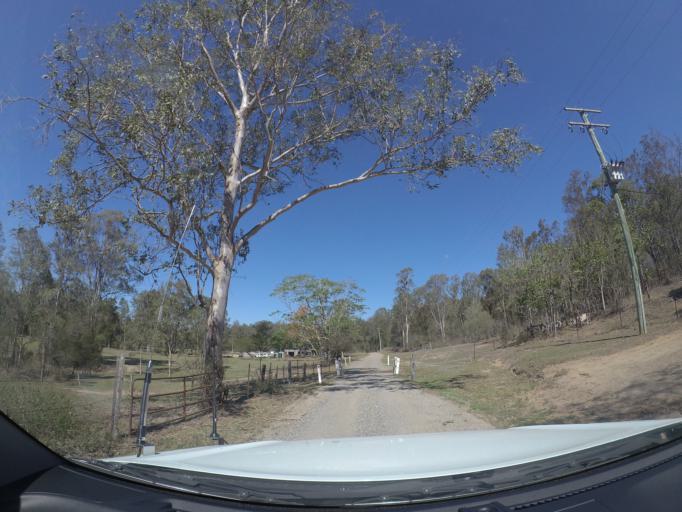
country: AU
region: Queensland
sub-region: Ipswich
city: Springfield Lakes
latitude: -27.7496
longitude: 152.8968
